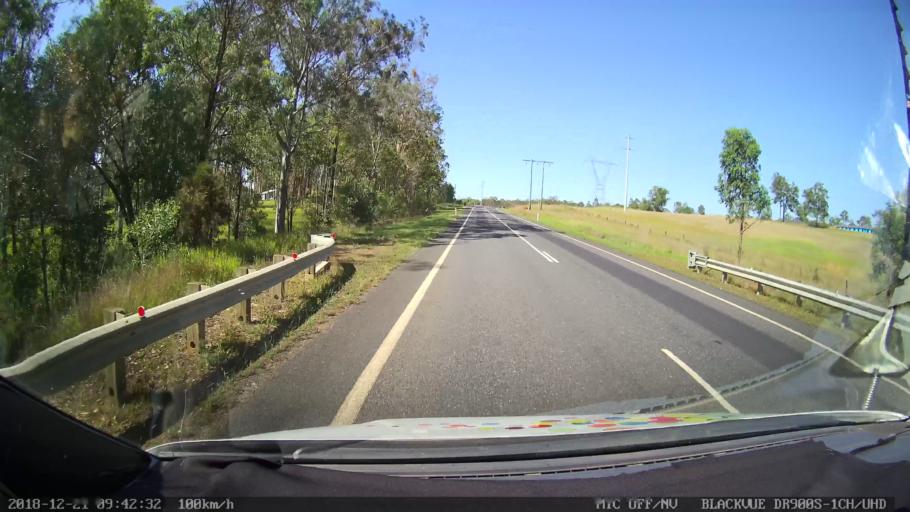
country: AU
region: New South Wales
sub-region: Clarence Valley
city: Grafton
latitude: -29.5976
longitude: 152.9458
